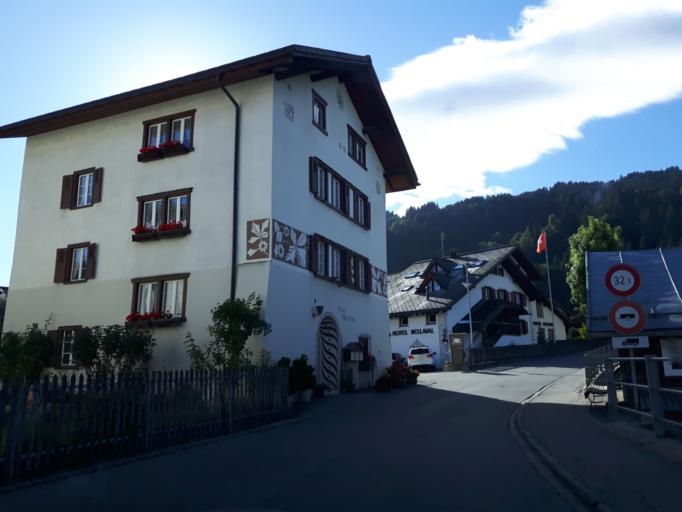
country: CH
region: Grisons
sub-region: Surselva District
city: Laax
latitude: 46.8060
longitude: 9.2565
